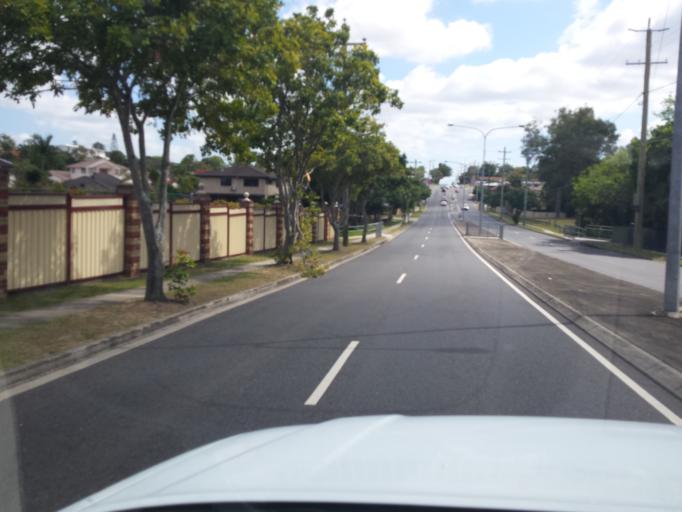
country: AU
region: Queensland
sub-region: Brisbane
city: Zillmere
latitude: -27.3696
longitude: 153.0363
